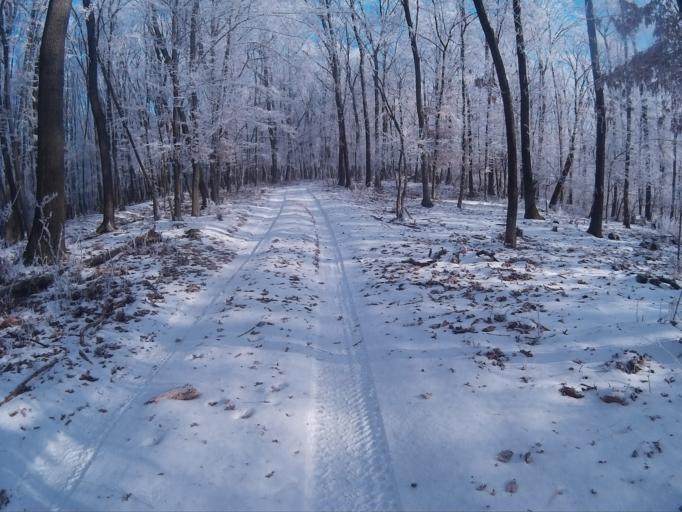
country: HU
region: Borsod-Abauj-Zemplen
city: Szendro
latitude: 48.4927
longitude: 20.7475
